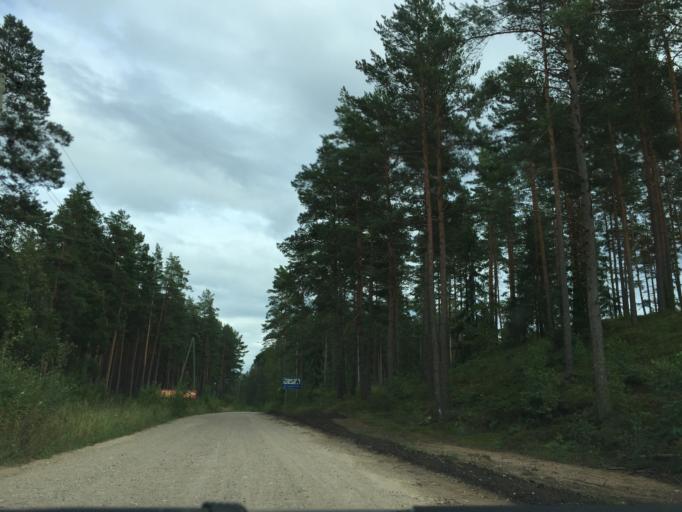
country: LV
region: Saulkrastu
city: Saulkrasti
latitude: 57.1915
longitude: 24.3549
